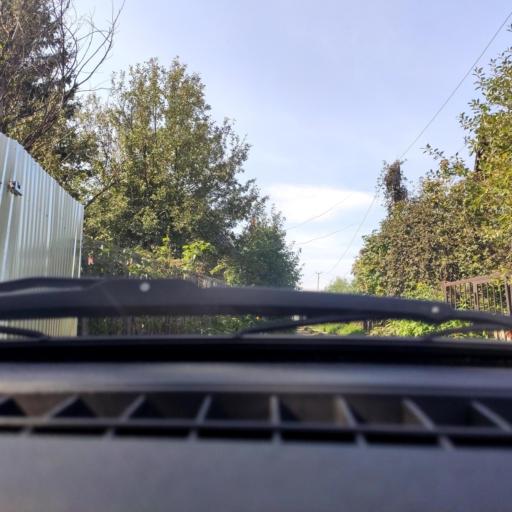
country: RU
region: Bashkortostan
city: Blagoveshchensk
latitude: 54.9433
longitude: 56.0896
